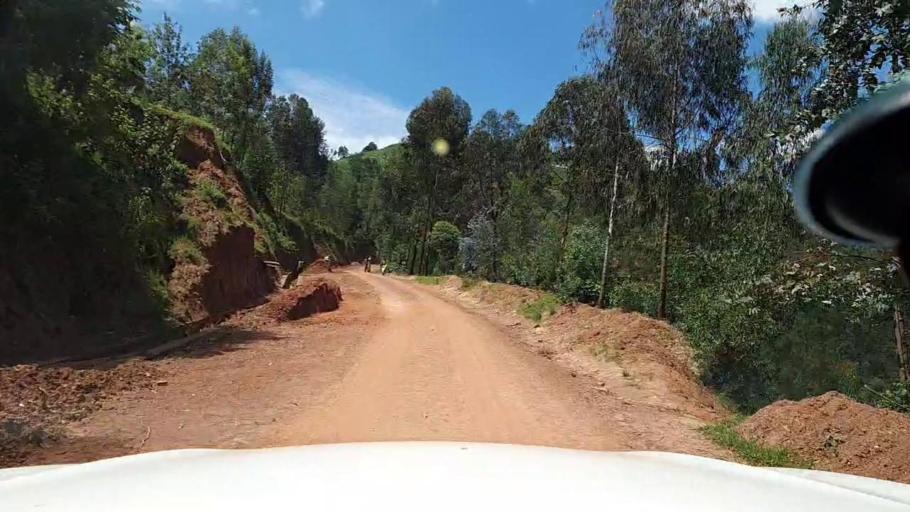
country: RW
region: Northern Province
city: Byumba
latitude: -1.7371
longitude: 29.8603
